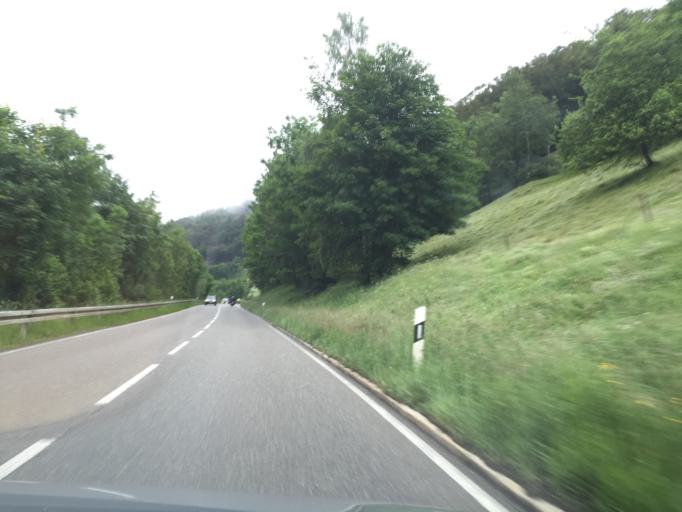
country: DE
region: Baden-Wuerttemberg
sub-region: Freiburg Region
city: Todtnau
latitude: 47.8350
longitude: 7.9381
